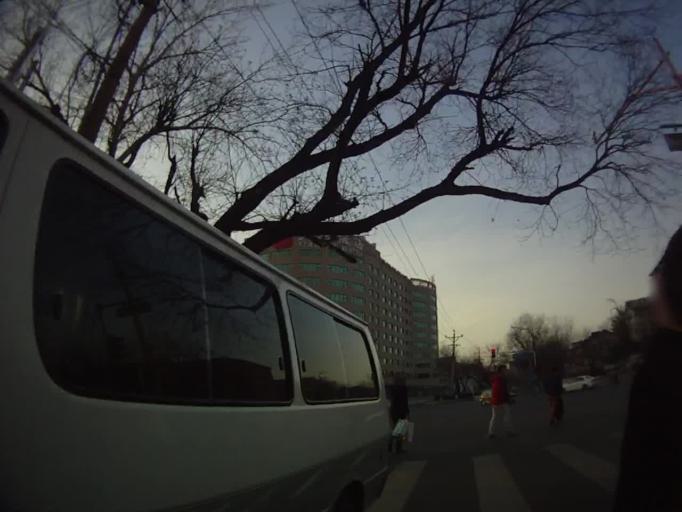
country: CN
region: Beijing
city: Longtan
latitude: 39.8825
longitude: 116.4253
